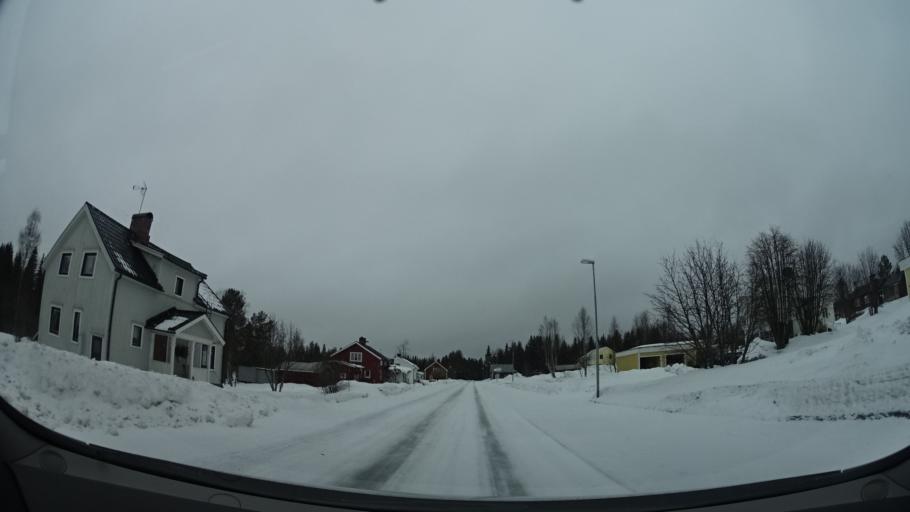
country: SE
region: Vaesterbotten
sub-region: Mala Kommun
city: Mala
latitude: 65.0875
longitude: 18.9563
